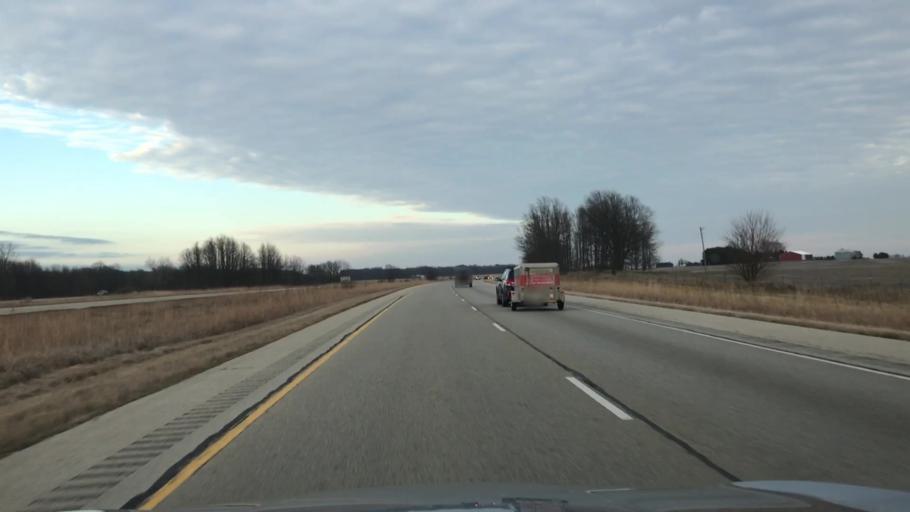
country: US
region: Illinois
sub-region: Logan County
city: Atlanta
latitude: 40.3429
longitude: -89.1348
